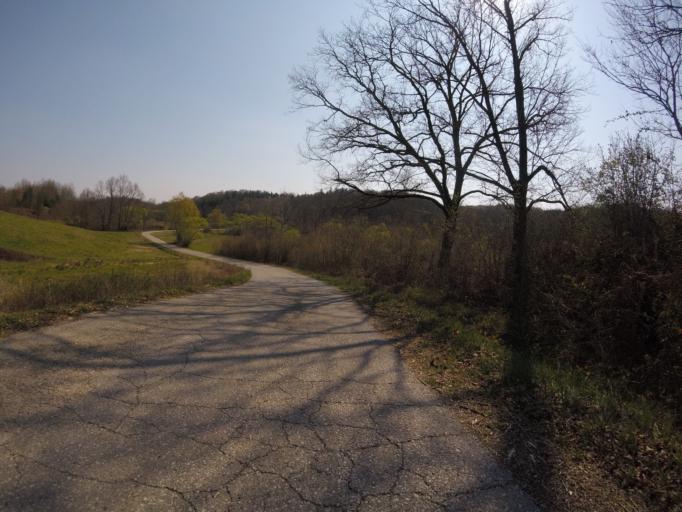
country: HR
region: Grad Zagreb
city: Strmec
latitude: 45.5847
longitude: 15.9215
